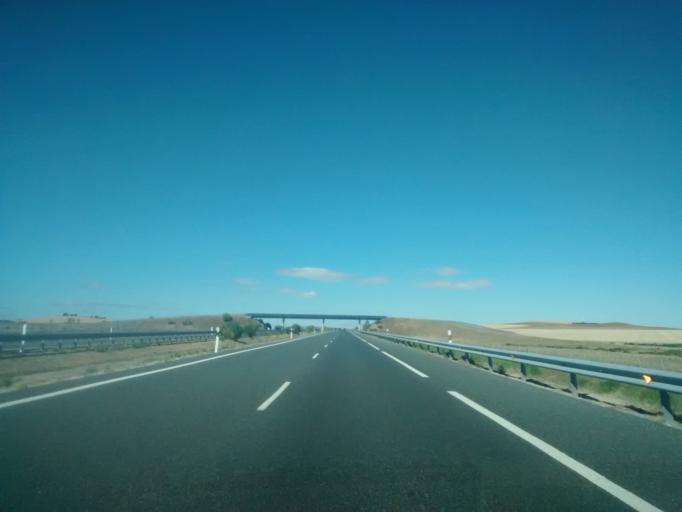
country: ES
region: Castille and Leon
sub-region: Provincia de Avila
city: Munosancho
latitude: 40.8881
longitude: -5.0262
